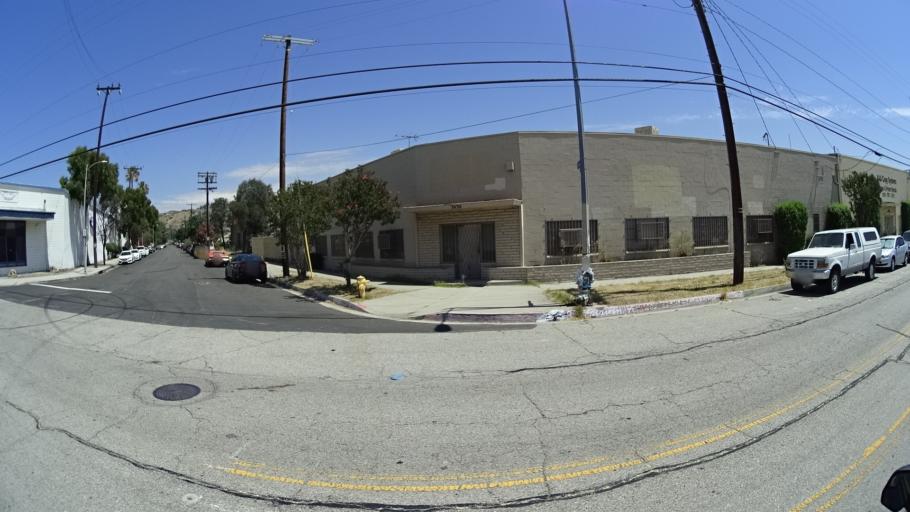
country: US
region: California
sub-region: Los Angeles County
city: North Hollywood
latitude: 34.2072
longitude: -118.3508
